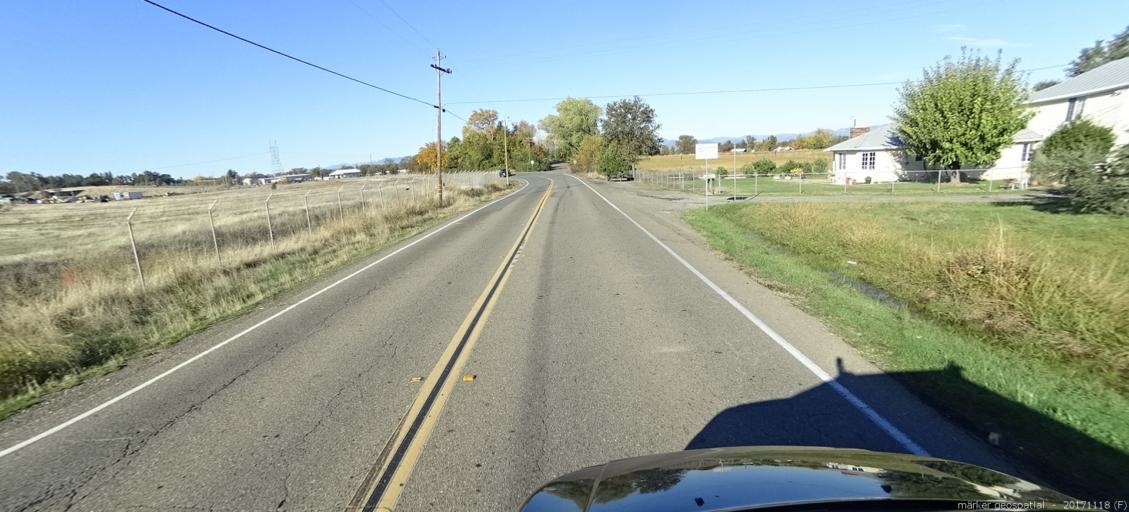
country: US
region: California
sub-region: Shasta County
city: Anderson
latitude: 40.4410
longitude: -122.2778
